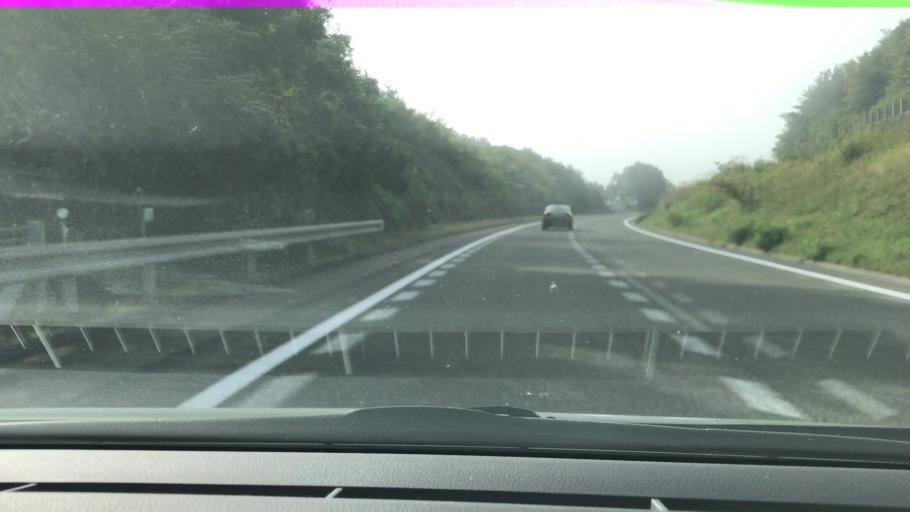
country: JP
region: Hyogo
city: Sasayama
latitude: 35.1043
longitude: 135.1708
